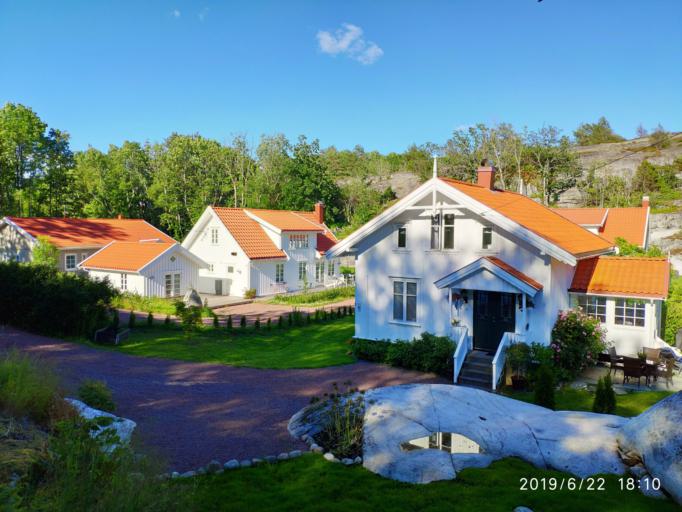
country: NO
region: Vestfold
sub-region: Tjome
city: Tjome
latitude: 59.0839
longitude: 10.4114
